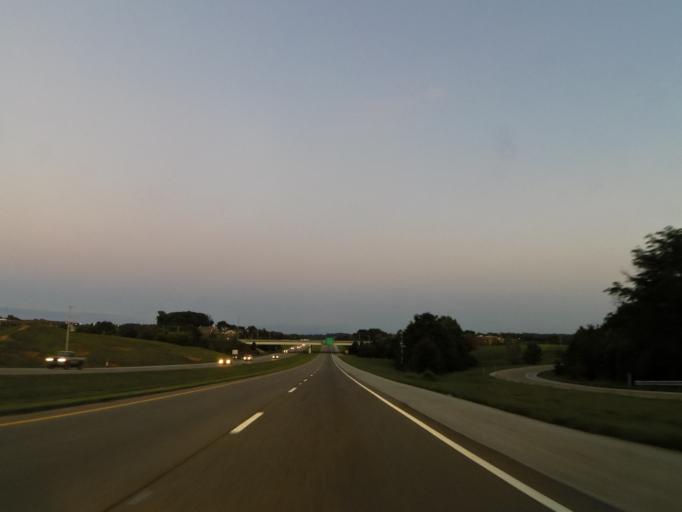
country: US
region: Tennessee
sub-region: Knox County
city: Farragut
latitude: 35.9273
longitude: -84.1361
